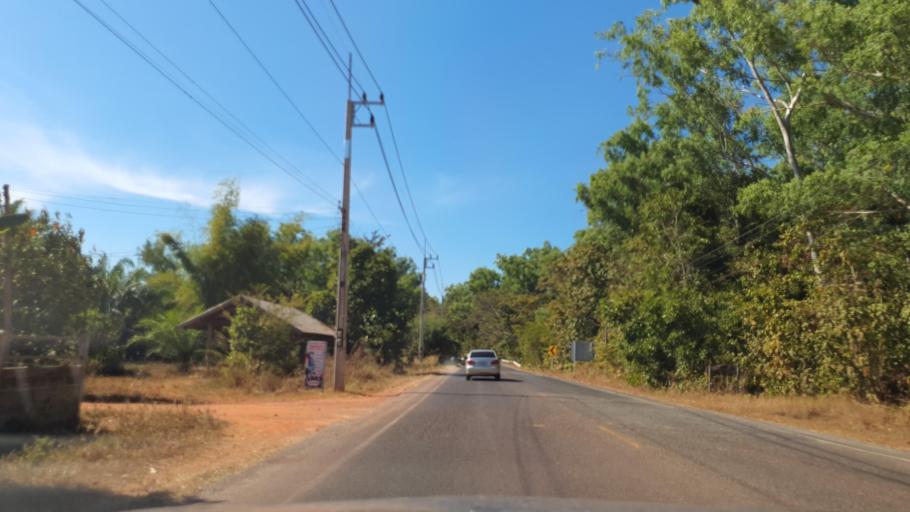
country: TH
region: Kalasin
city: Khao Wong
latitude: 16.7635
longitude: 104.1470
